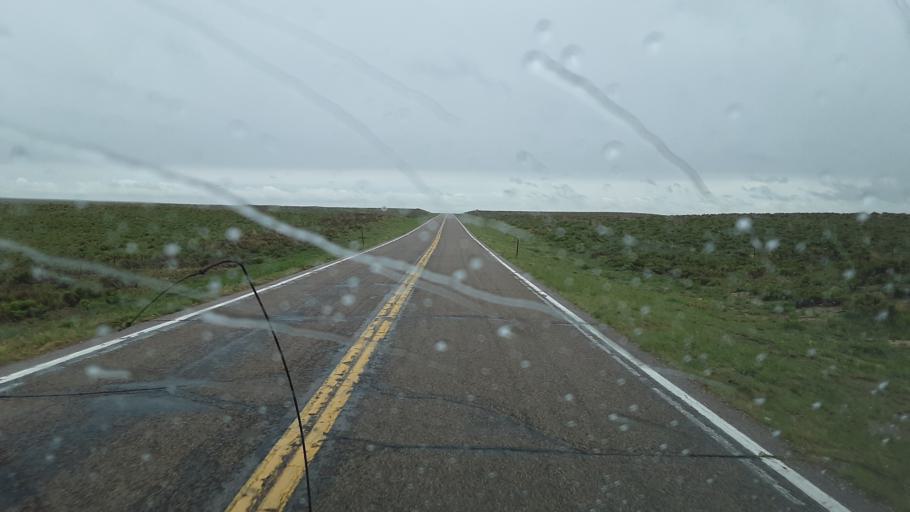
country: US
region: Colorado
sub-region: Lincoln County
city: Hugo
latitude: 38.8495
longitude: -103.1648
